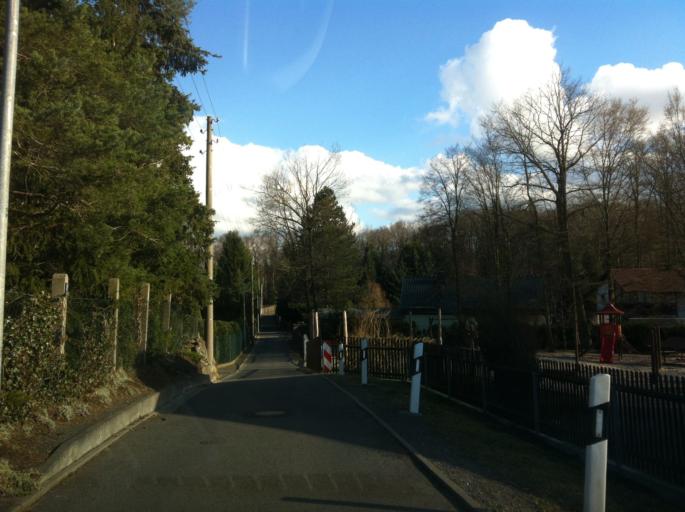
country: DE
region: Saxony
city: Bennewitz
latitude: 51.3488
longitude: 12.7022
